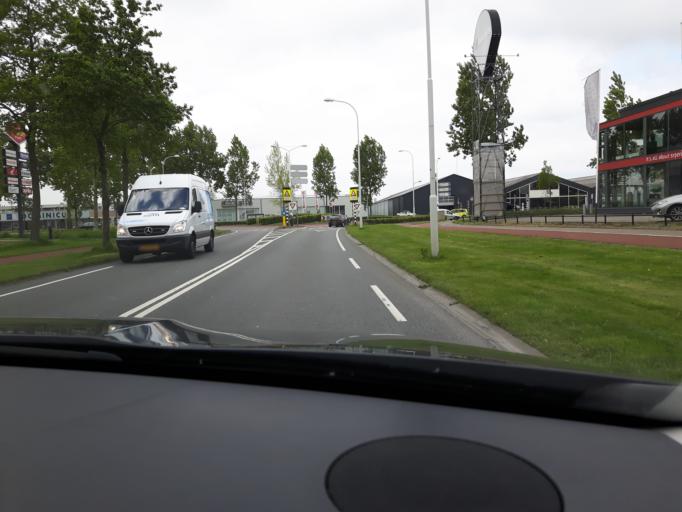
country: NL
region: Zeeland
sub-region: Gemeente Goes
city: Goes
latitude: 51.4917
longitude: 3.8769
